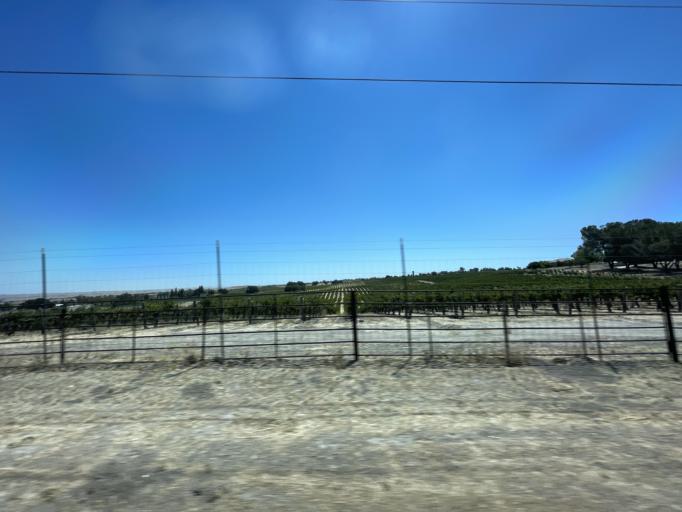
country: US
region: California
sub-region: San Luis Obispo County
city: Paso Robles
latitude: 35.6475
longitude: -120.5787
